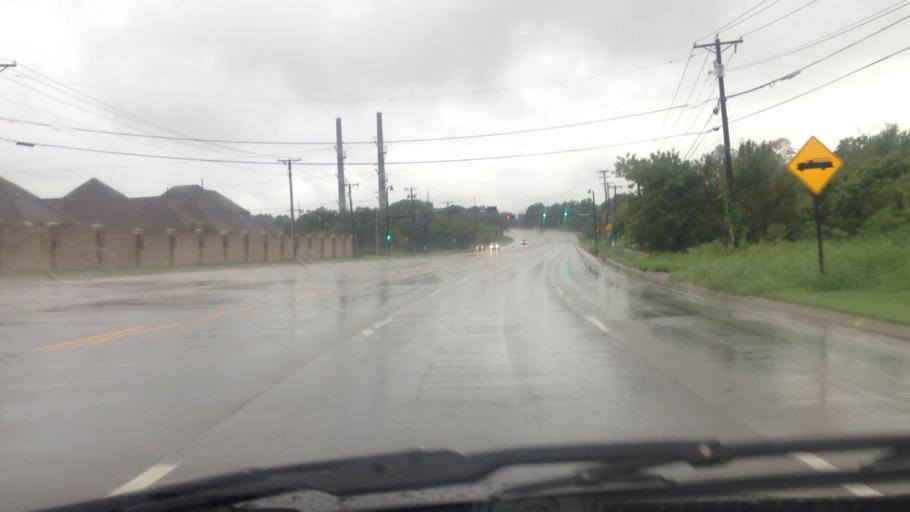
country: US
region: Texas
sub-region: Tarrant County
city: Colleyville
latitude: 32.8970
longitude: -97.1986
